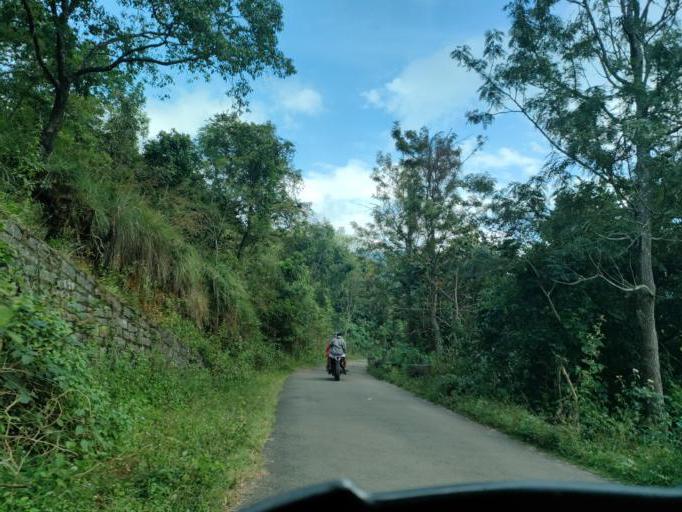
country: IN
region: Tamil Nadu
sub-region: Dindigul
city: Kodaikanal
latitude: 10.2892
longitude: 77.5277
